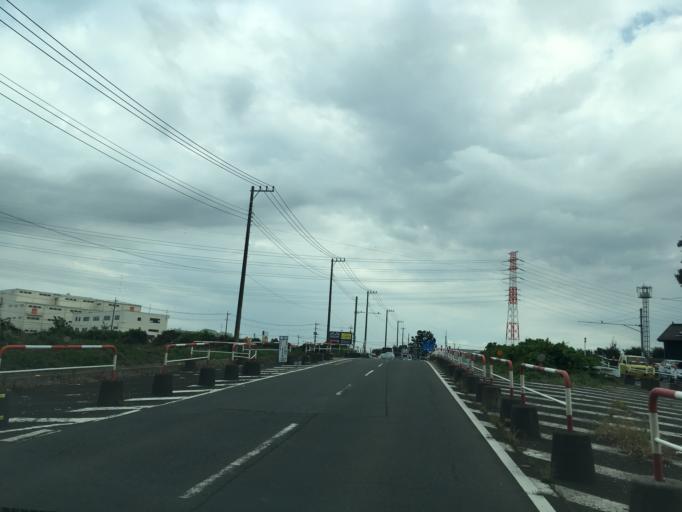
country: JP
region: Saitama
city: Tokorozawa
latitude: 35.8024
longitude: 139.4982
